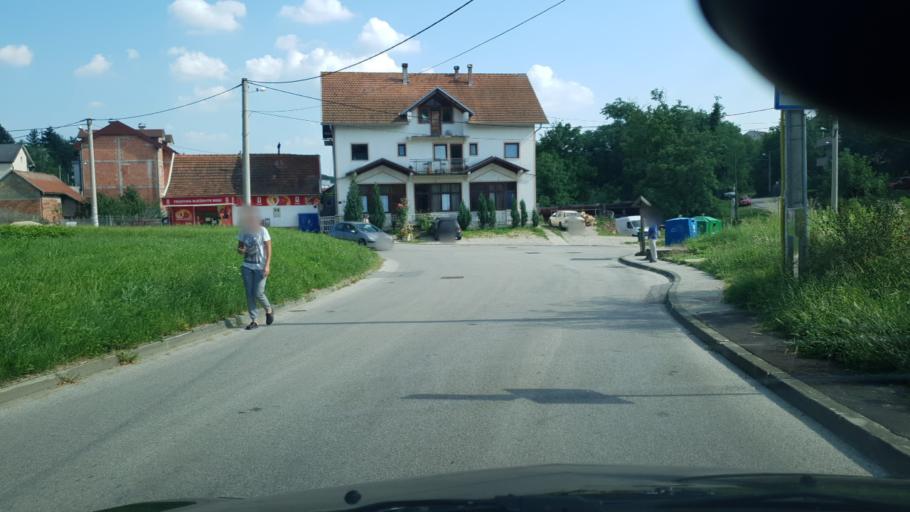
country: HR
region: Grad Zagreb
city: Stenjevec
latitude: 45.8373
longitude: 15.9193
